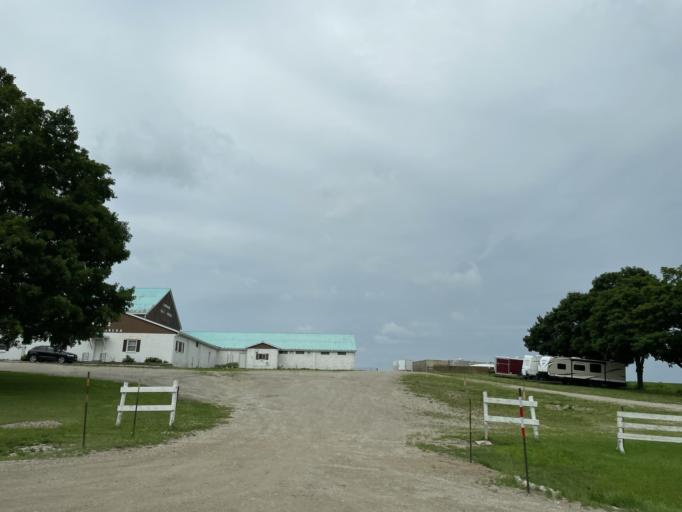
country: CA
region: Ontario
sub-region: Wellington County
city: Guelph
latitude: 43.5474
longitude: -80.3265
